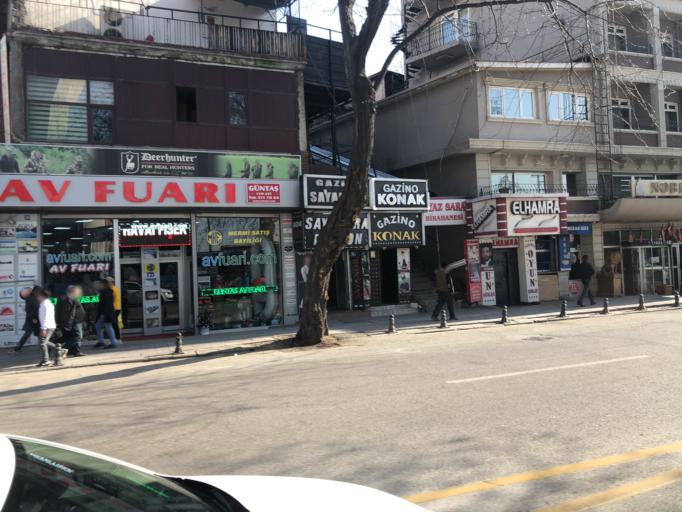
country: TR
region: Ankara
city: Ankara
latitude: 39.9487
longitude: 32.8565
